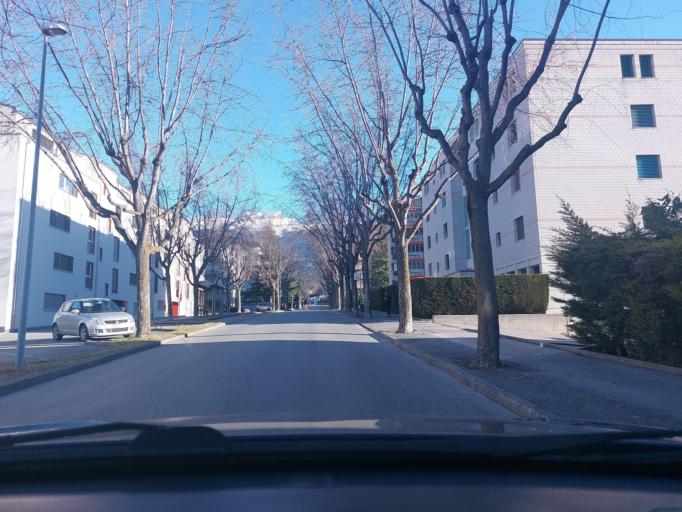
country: CH
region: Valais
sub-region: Sierre District
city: Chalais
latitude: 46.2835
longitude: 7.5183
